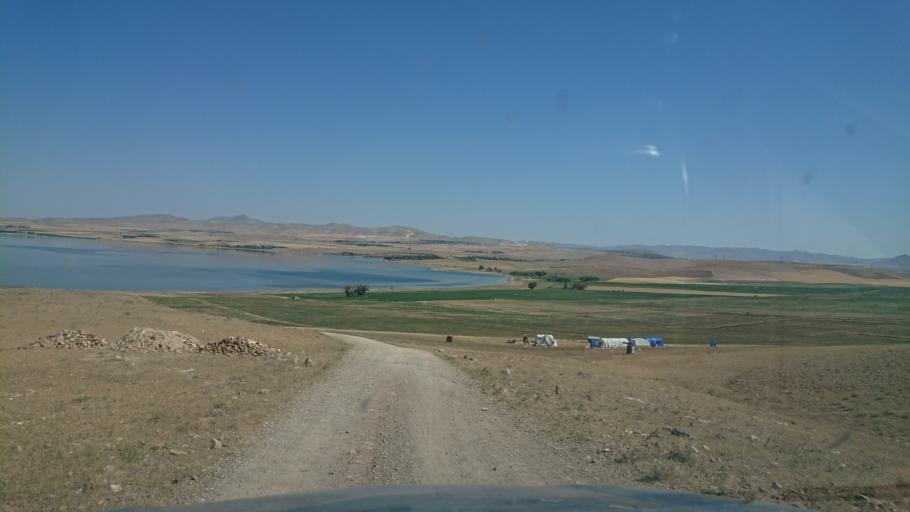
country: TR
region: Aksaray
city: Sariyahsi
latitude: 39.0545
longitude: 33.8849
